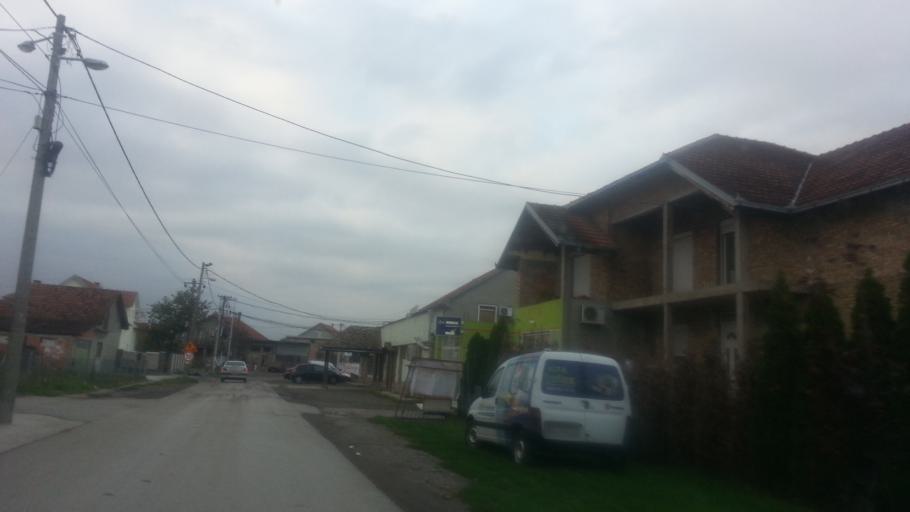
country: RS
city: Novi Banovci
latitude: 44.9148
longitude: 20.2716
